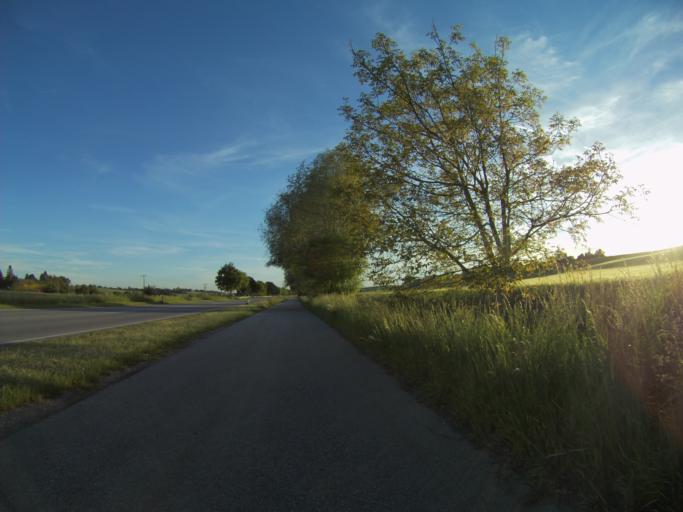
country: DE
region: Bavaria
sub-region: Upper Bavaria
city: Marzling
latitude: 48.4214
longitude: 11.8194
